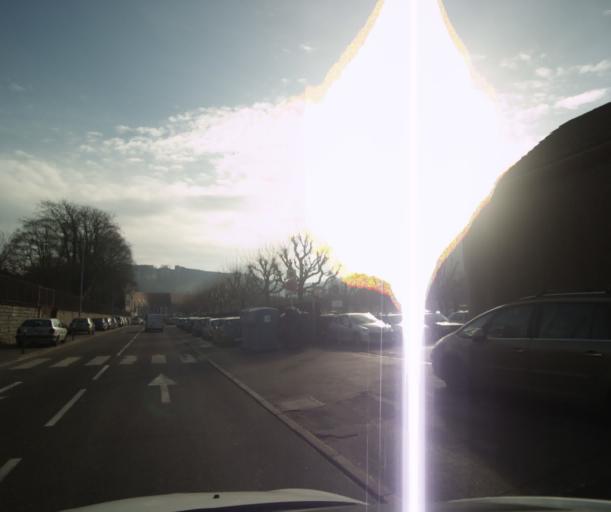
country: FR
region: Franche-Comte
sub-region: Departement du Doubs
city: Besancon
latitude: 47.2327
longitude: 6.0208
